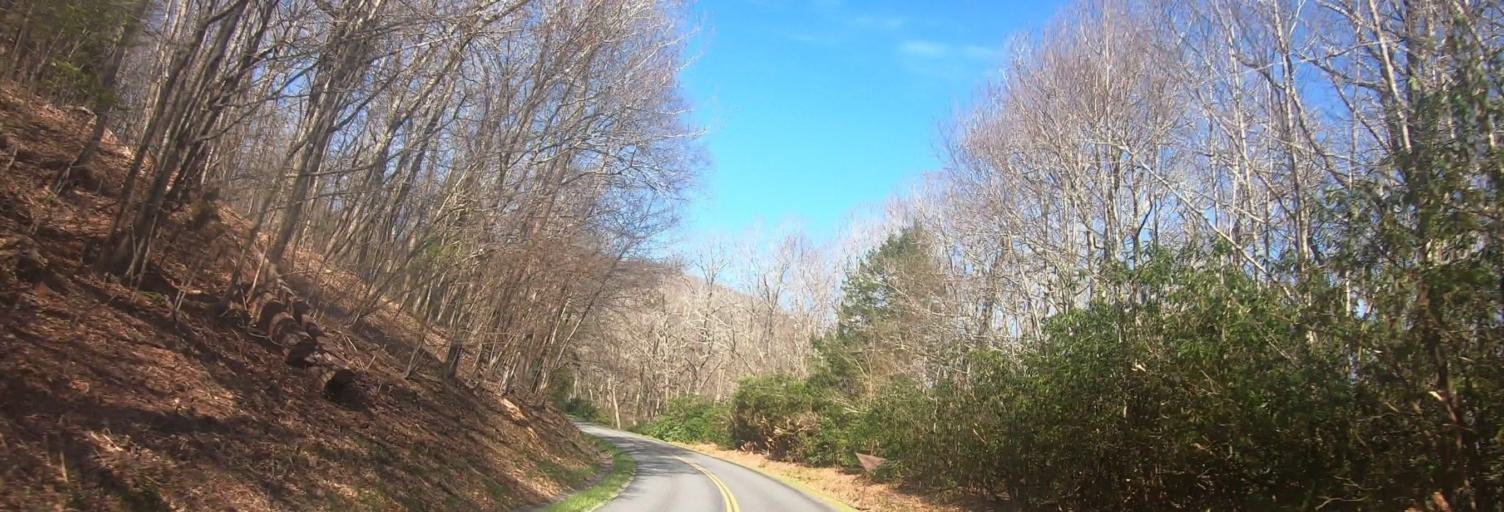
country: US
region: North Carolina
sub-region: Avery County
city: Newland
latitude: 36.0510
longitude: -81.8544
